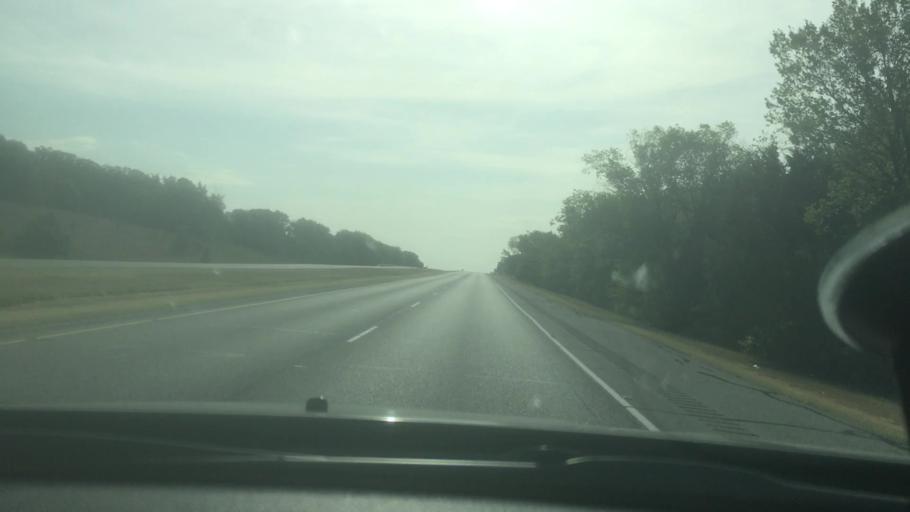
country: US
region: Oklahoma
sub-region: Carter County
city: Ardmore
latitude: 34.1392
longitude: -97.1522
